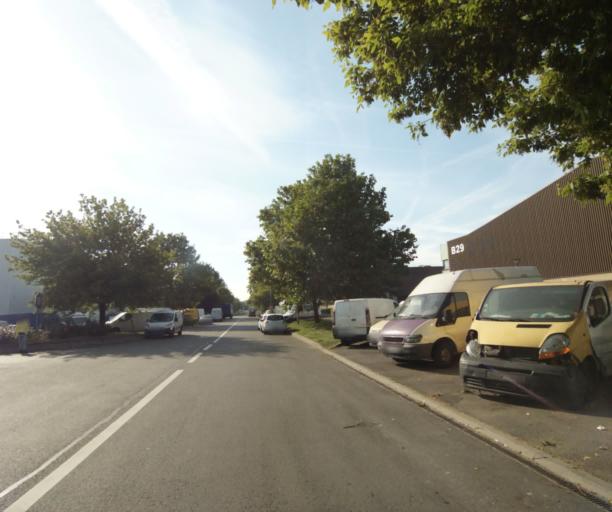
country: FR
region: Ile-de-France
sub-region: Departement des Hauts-de-Seine
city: Bois-Colombes
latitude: 48.9411
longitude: 2.2777
